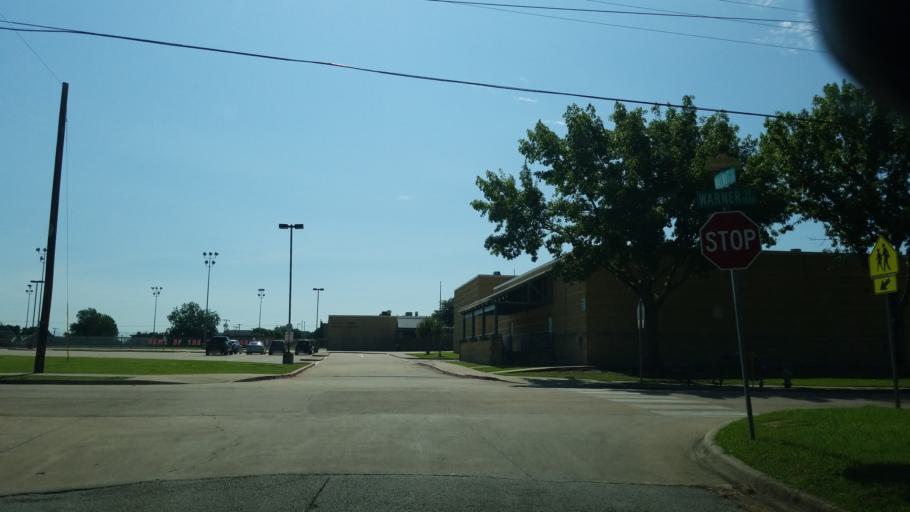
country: US
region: Texas
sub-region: Dallas County
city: Carrollton
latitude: 32.9550
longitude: -96.8982
